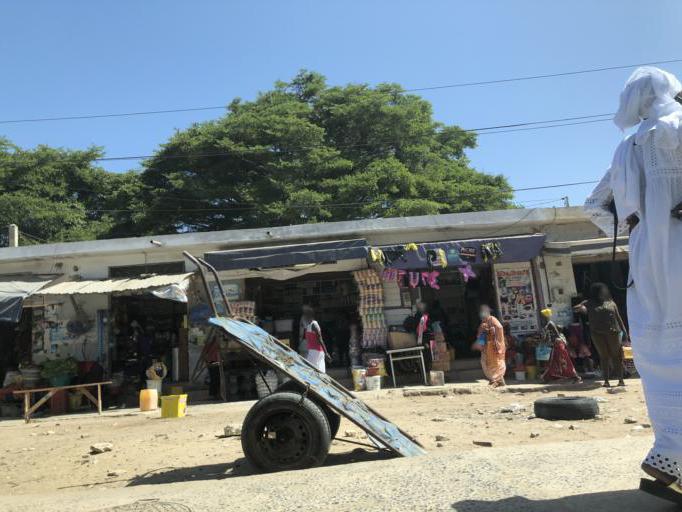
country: SN
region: Dakar
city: Mermoz Boabab
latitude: 14.7242
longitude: -17.4879
